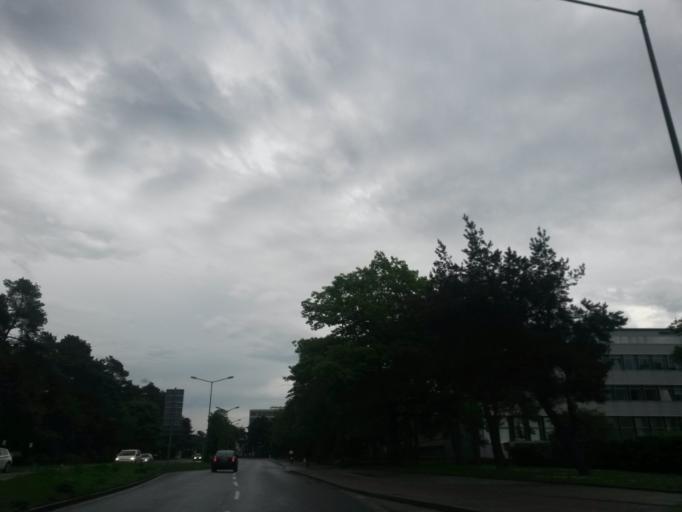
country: DE
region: Bavaria
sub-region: Regierungsbezirk Mittelfranken
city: Erlangen
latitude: 49.5773
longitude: 11.0048
